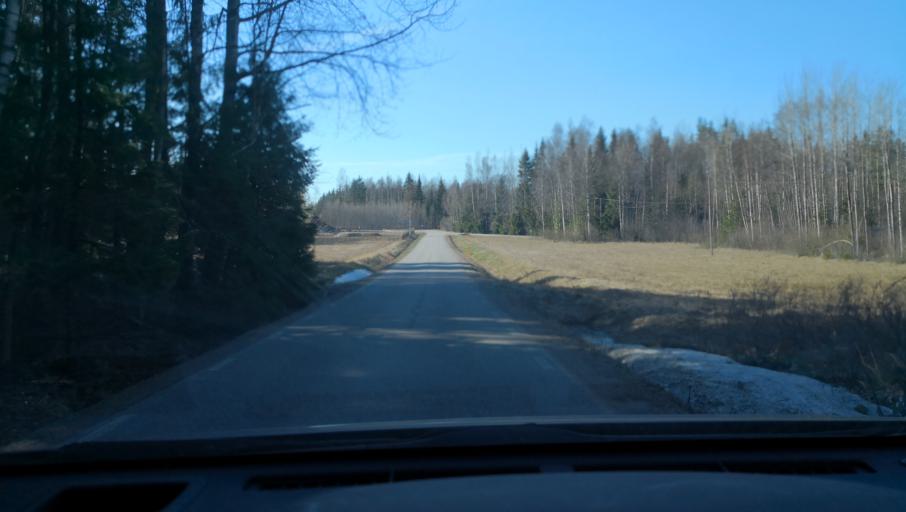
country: SE
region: Dalarna
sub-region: Avesta Kommun
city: Horndal
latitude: 60.0879
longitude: 16.4077
